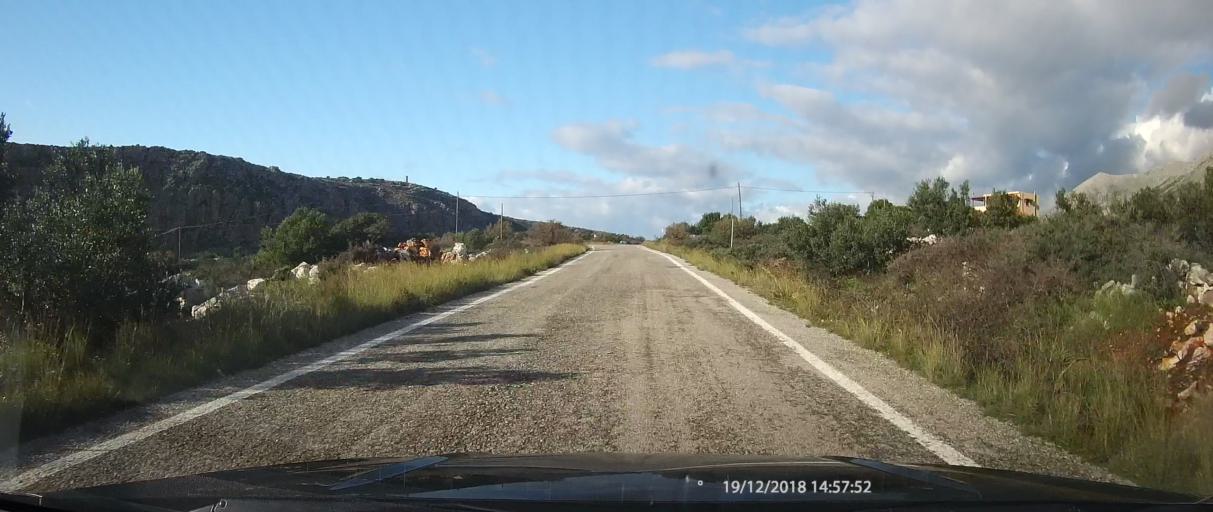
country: GR
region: Peloponnese
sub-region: Nomos Lakonias
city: Gytheio
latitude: 36.4831
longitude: 22.4041
